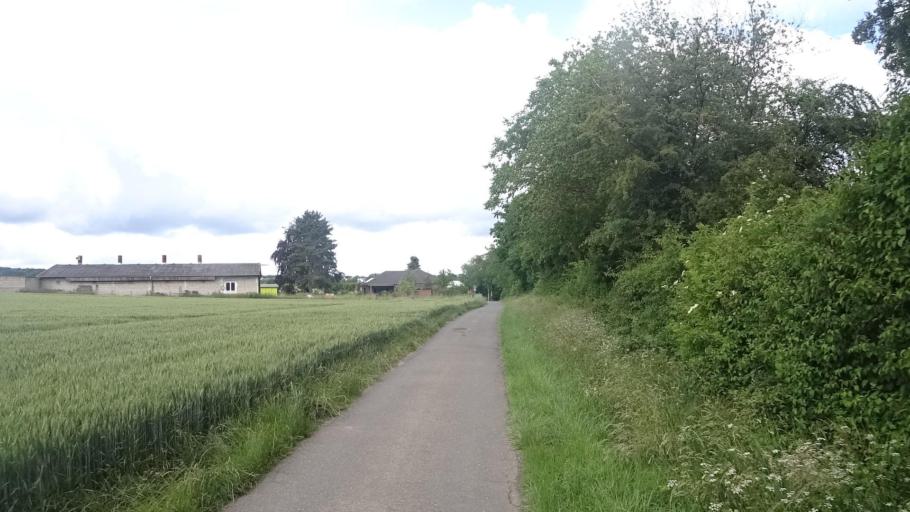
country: DE
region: Rheinland-Pfalz
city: Bad Neuenahr-Ahrweiler
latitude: 50.5683
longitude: 7.0991
